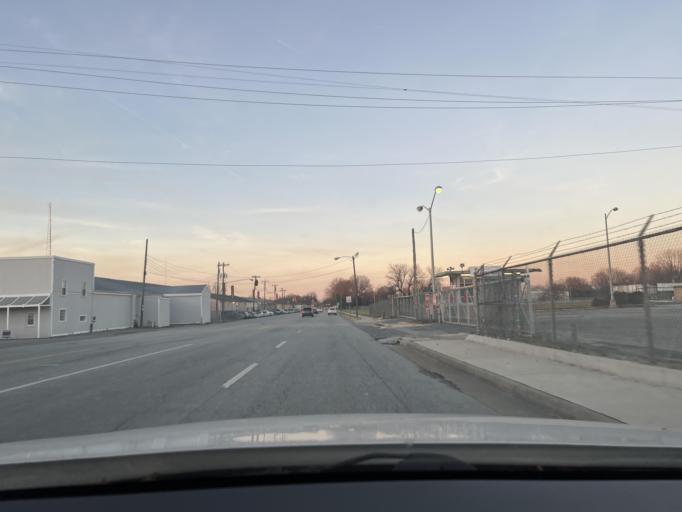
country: US
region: North Carolina
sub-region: Guilford County
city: Greensboro
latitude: 36.0800
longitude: -79.7573
